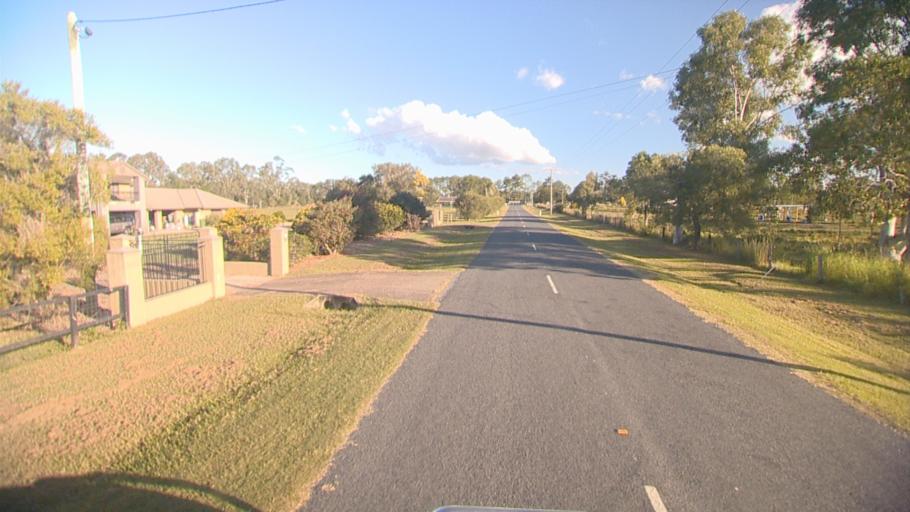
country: AU
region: Queensland
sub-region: Gold Coast
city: Yatala
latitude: -27.6759
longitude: 153.2431
